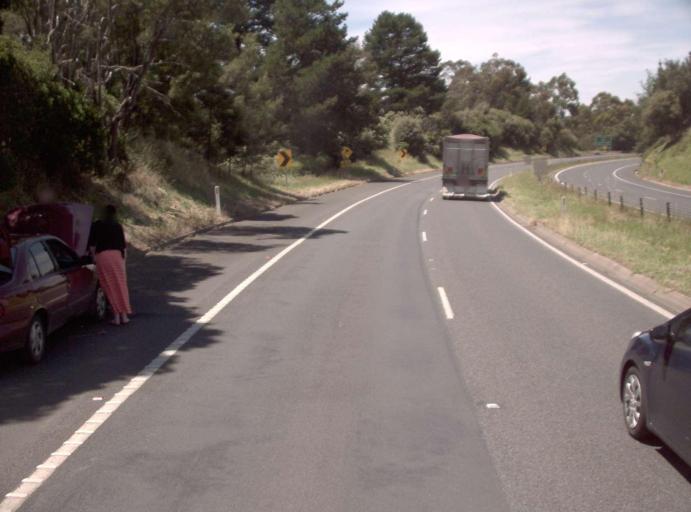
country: AU
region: Victoria
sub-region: Latrobe
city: Moe
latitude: -38.1820
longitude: 146.2686
